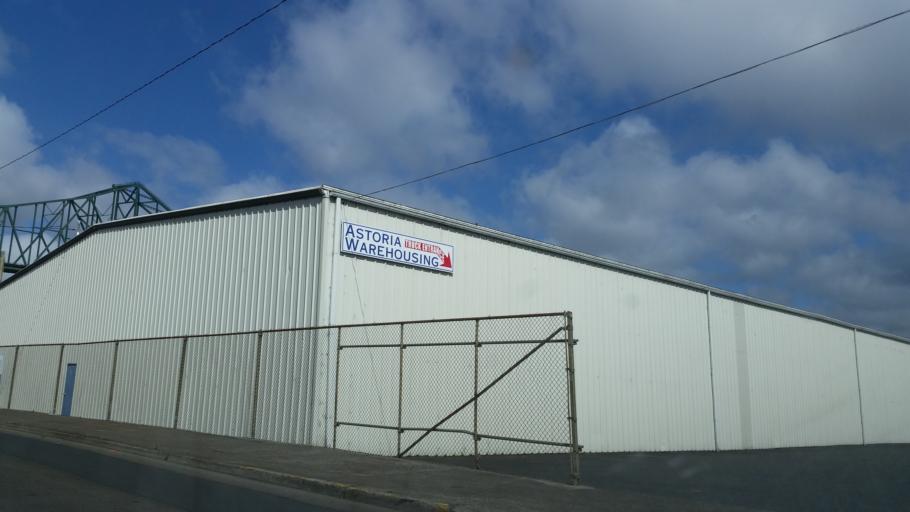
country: US
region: Oregon
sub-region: Clatsop County
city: Astoria
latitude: 46.1906
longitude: -123.8450
